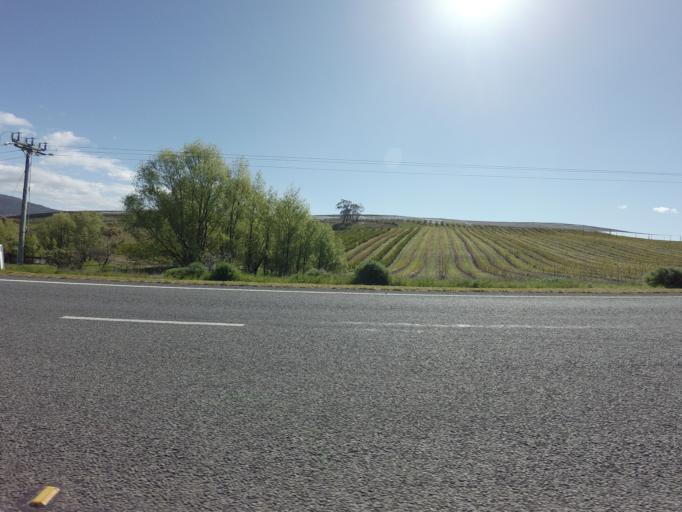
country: AU
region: Tasmania
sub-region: Derwent Valley
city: New Norfolk
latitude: -42.7136
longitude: 146.9466
